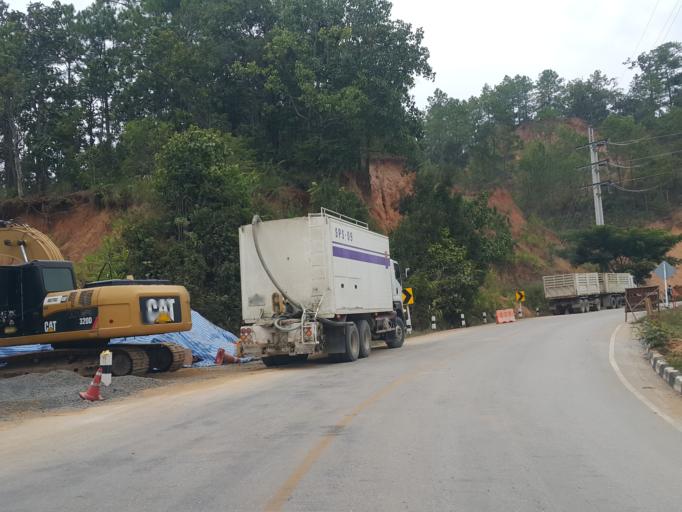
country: TH
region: Mae Hong Son
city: Mae Hi
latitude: 19.2696
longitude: 98.5323
